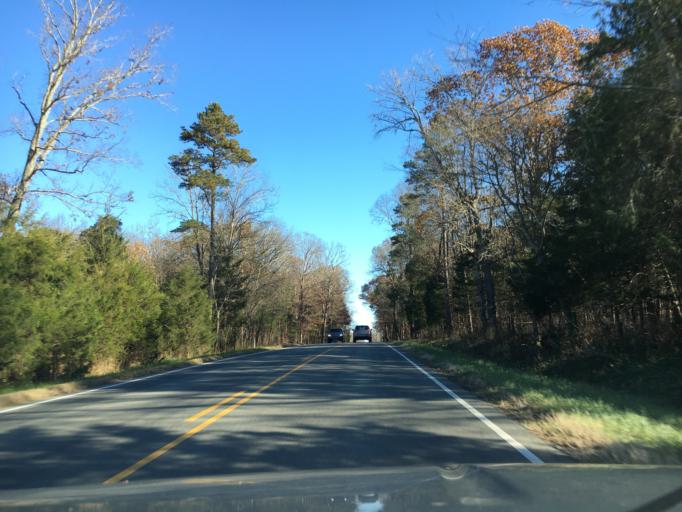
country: US
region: Virginia
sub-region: Buckingham County
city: Buckingham
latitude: 37.5423
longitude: -78.6077
